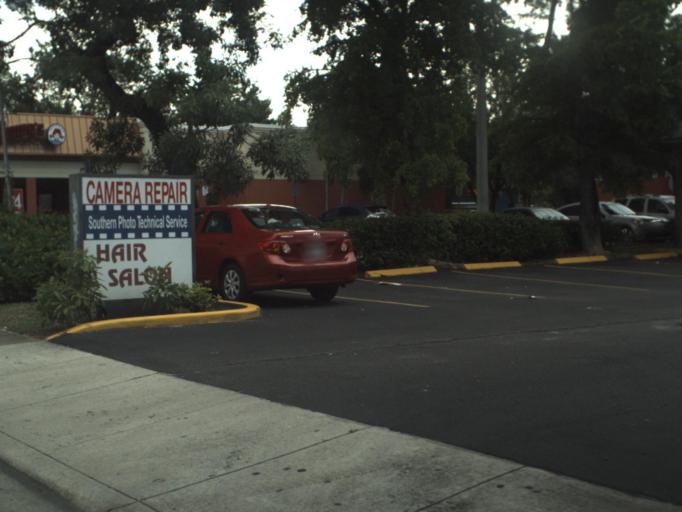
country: US
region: Florida
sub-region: Miami-Dade County
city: Golden Glades
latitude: 25.9282
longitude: -80.1993
